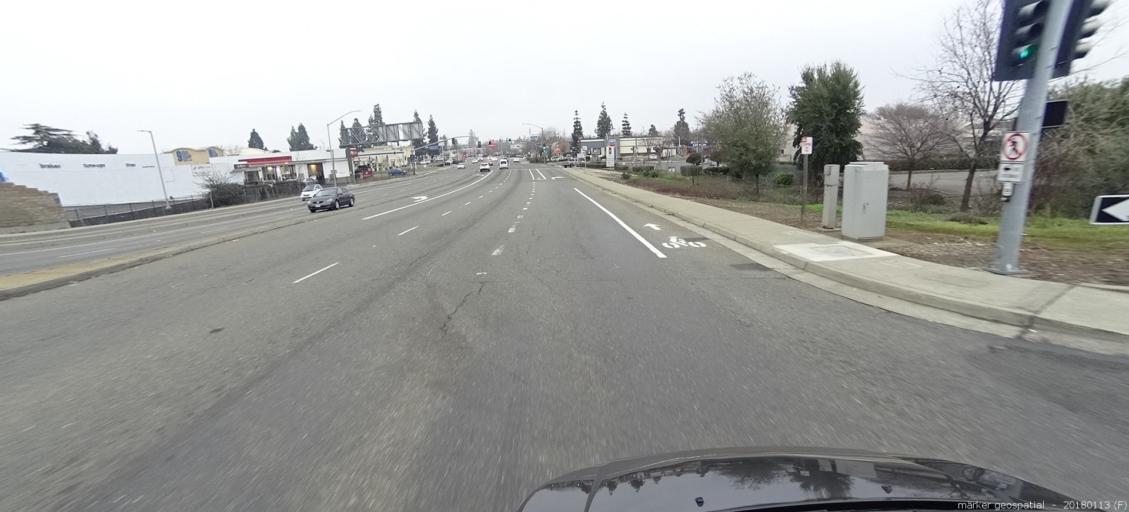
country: US
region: California
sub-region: Sacramento County
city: Rancho Cordova
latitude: 38.5925
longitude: -121.2876
